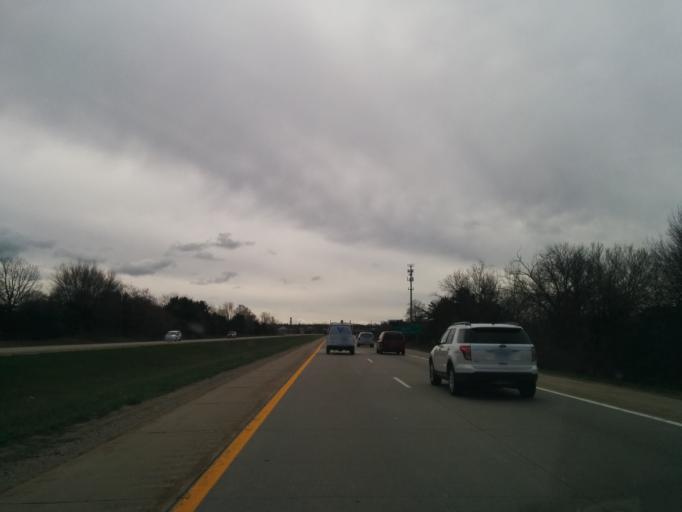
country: US
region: Michigan
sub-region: Ottawa County
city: Jenison
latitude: 42.8935
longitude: -85.7801
